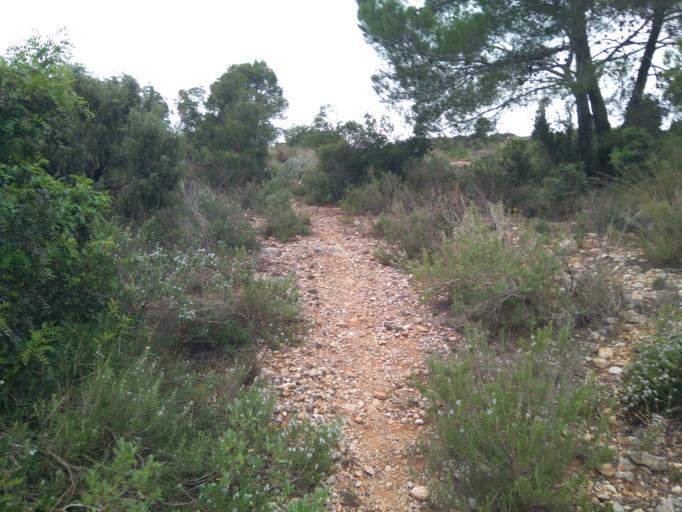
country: ES
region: Valencia
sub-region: Provincia de Valencia
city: Benimodo
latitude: 39.1973
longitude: -0.5743
